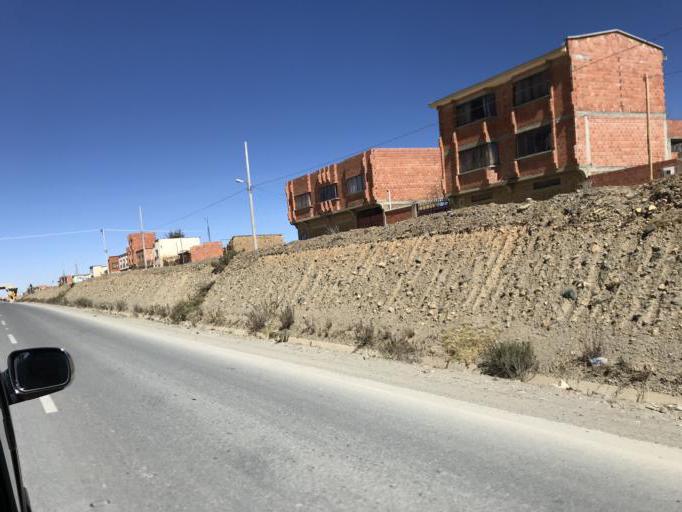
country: BO
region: La Paz
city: Batallas
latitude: -16.3342
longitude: -68.4175
